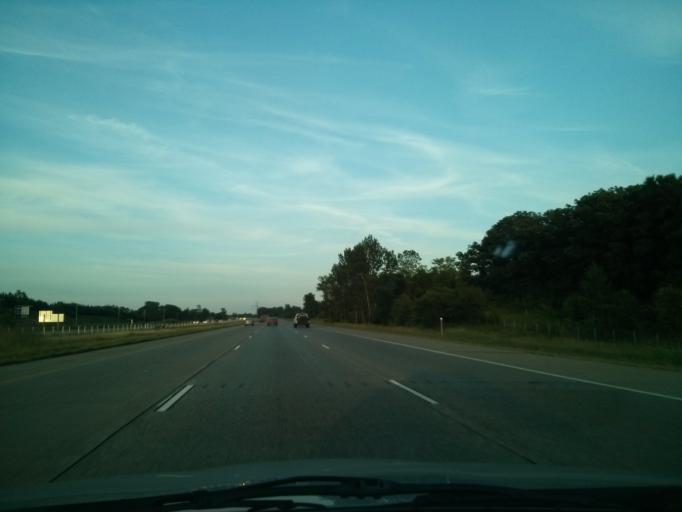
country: US
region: Minnesota
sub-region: Washington County
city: Lake Elmo
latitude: 44.9485
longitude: -92.8385
